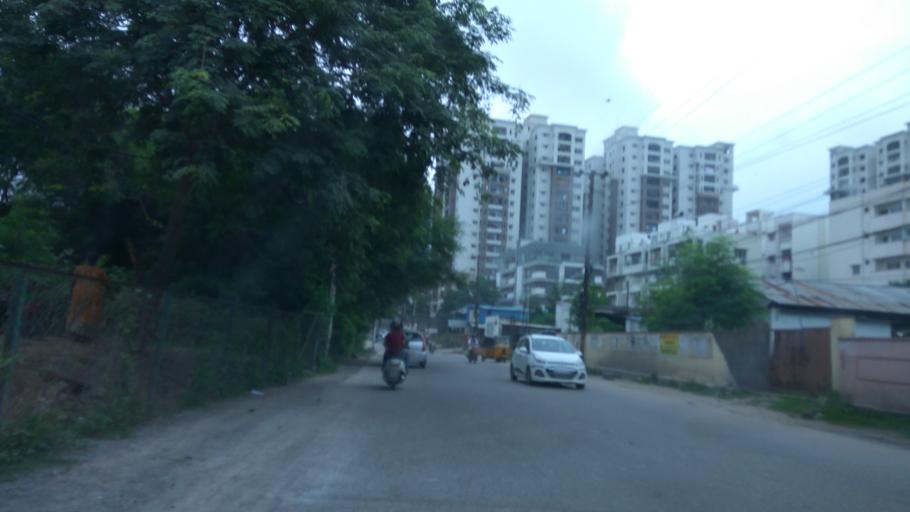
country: IN
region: Telangana
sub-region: Rangareddi
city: Kukatpalli
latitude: 17.4382
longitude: 78.3919
